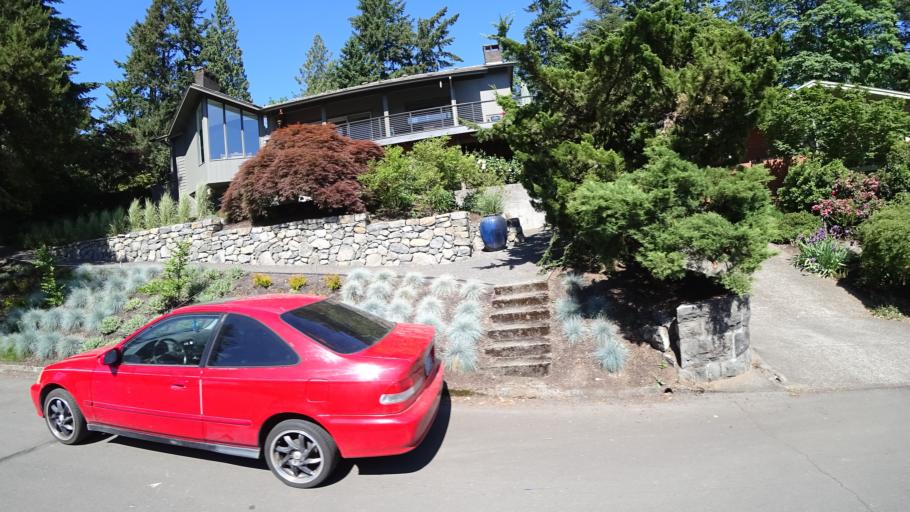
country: US
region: Oregon
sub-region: Washington County
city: West Slope
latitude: 45.4973
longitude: -122.7266
